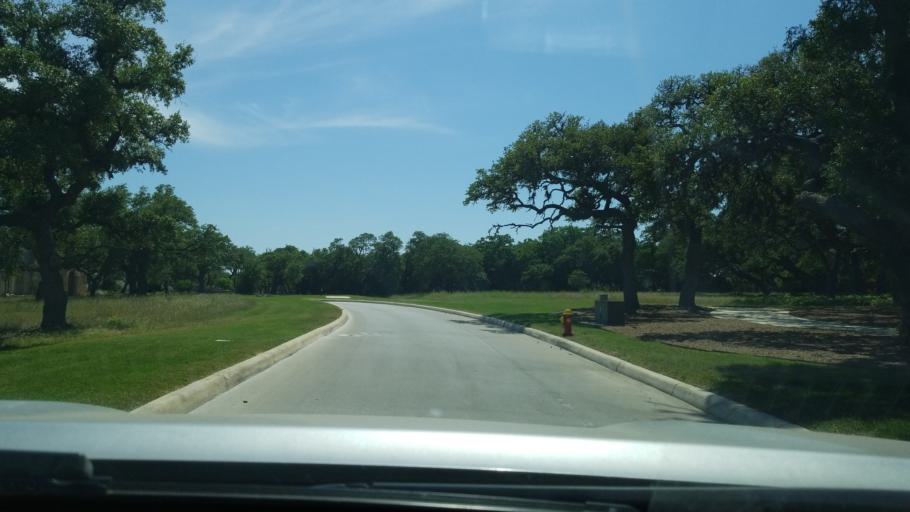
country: US
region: Texas
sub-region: Kendall County
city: Boerne
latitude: 29.7891
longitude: -98.6924
